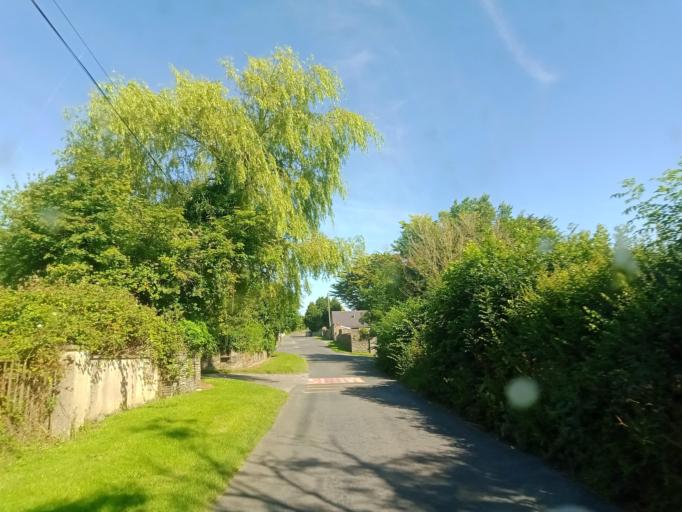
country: IE
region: Leinster
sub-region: Kilkenny
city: Ballyragget
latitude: 52.7567
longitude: -7.4032
